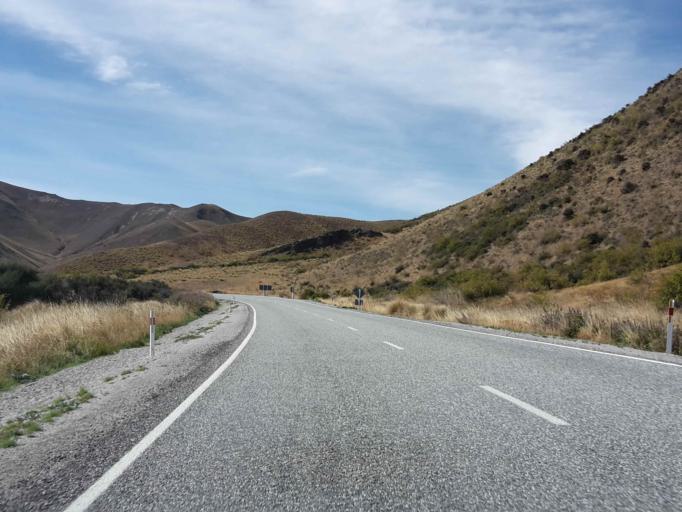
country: NZ
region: Otago
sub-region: Queenstown-Lakes District
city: Wanaka
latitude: -44.5799
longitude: 169.6108
